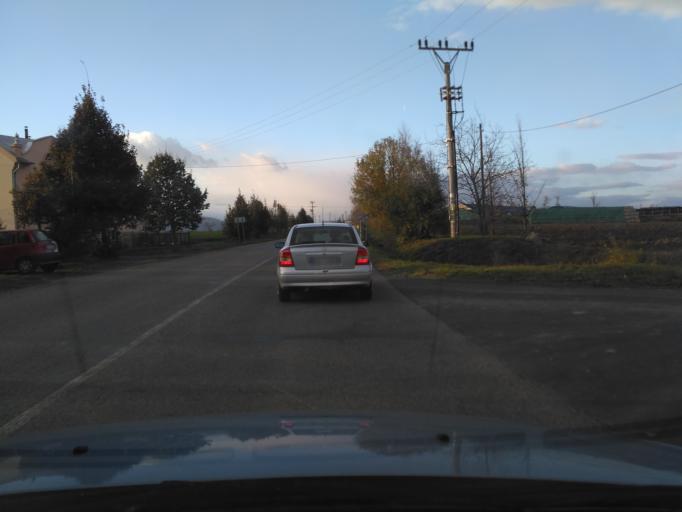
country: SK
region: Kosicky
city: Secovce
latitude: 48.6536
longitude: 21.6744
